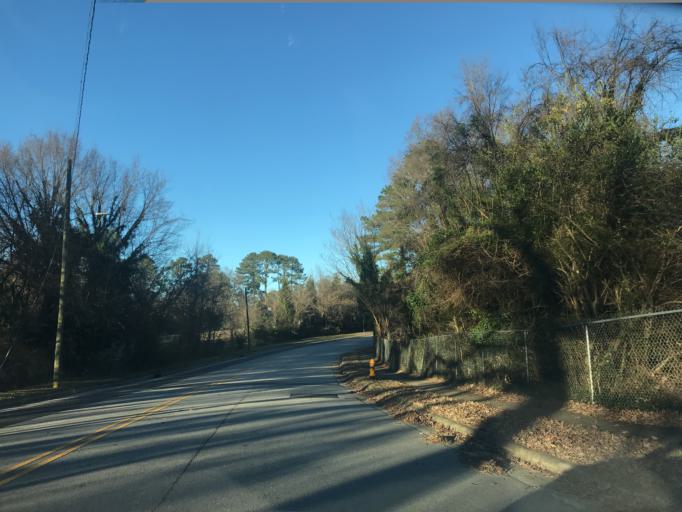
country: US
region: North Carolina
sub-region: Wake County
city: Raleigh
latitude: 35.7858
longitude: -78.6233
